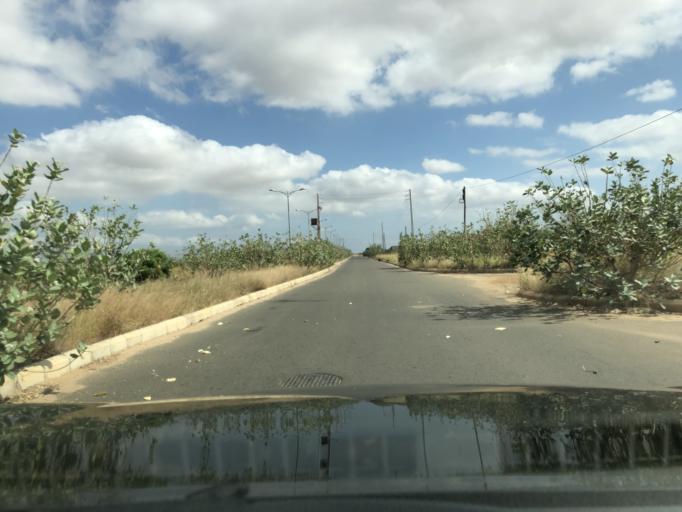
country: AO
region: Luanda
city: Luanda
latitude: -8.9606
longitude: 13.2414
